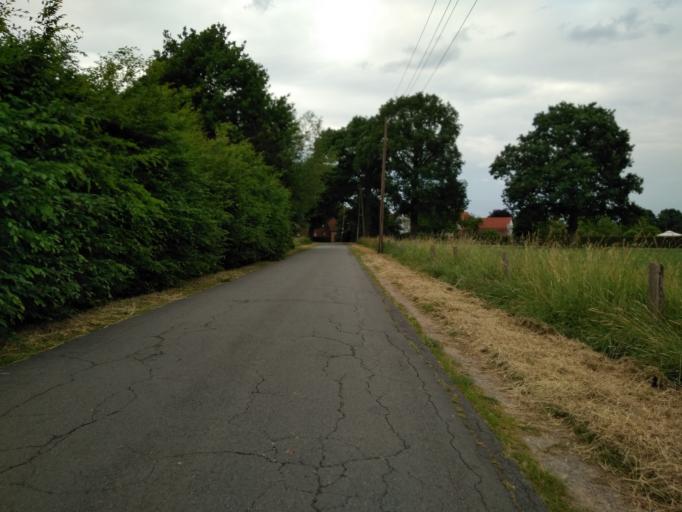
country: DE
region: North Rhine-Westphalia
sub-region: Regierungsbezirk Dusseldorf
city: Schermbeck
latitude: 51.6669
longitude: 6.8641
